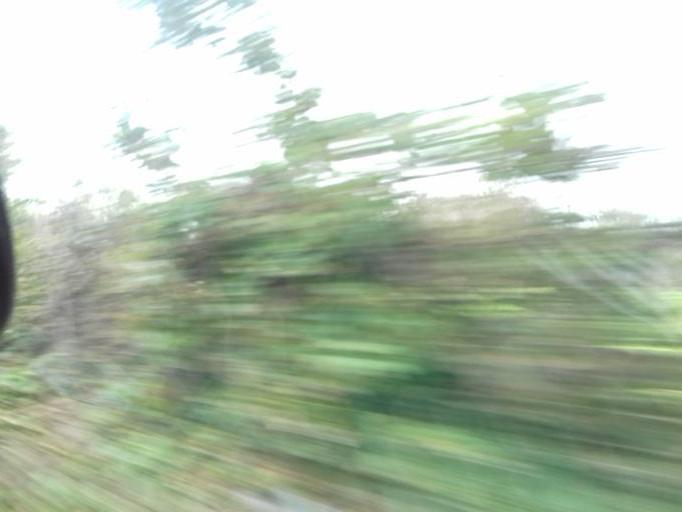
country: IE
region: Leinster
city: Donaghmede
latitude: 53.4240
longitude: -6.1654
